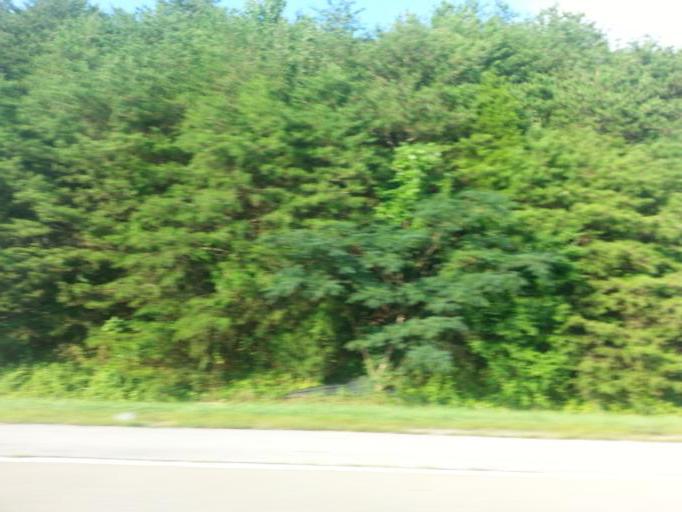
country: US
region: Tennessee
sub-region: Knox County
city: Farragut
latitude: 35.8802
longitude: -84.0980
